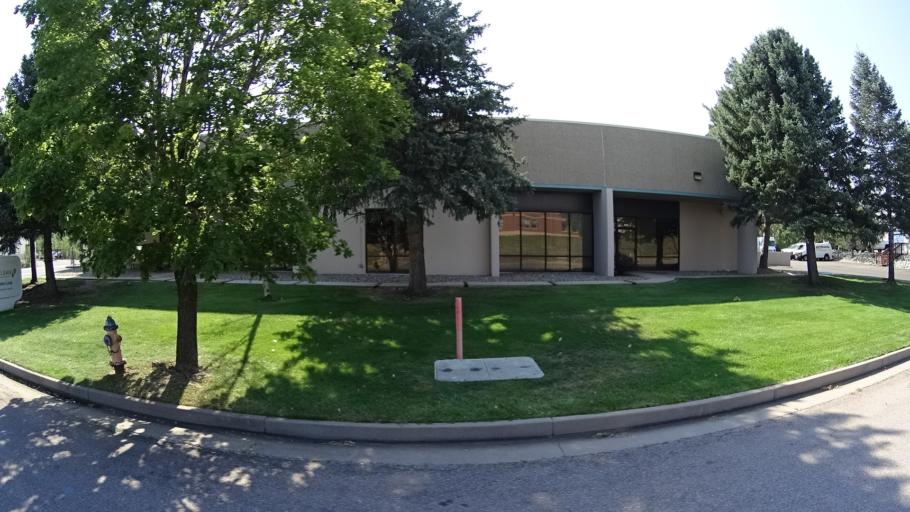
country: US
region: Colorado
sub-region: El Paso County
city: Stratmoor
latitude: 38.7881
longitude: -104.8007
